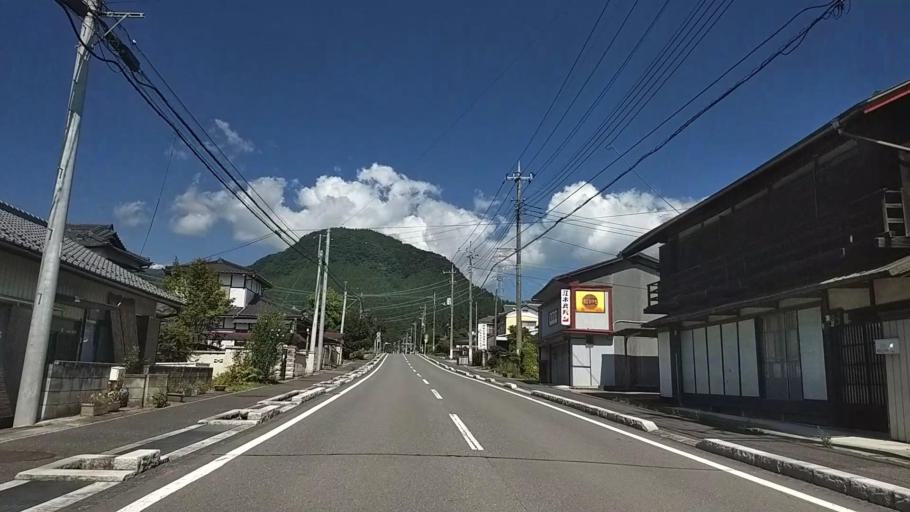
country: JP
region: Gunma
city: Annaka
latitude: 36.3475
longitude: 138.7200
